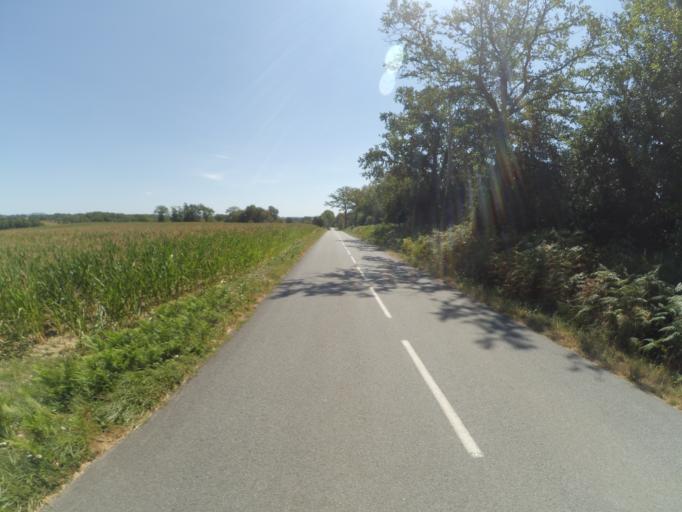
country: FR
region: Limousin
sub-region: Departement de la Creuse
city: Le Grand-Bourg
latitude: 46.2095
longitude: 1.5945
